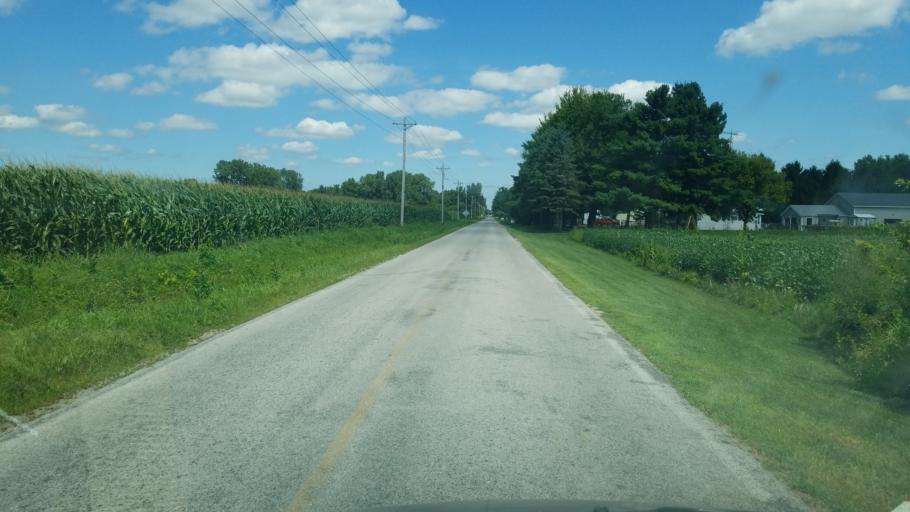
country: US
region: Ohio
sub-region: Fulton County
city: Delta
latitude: 41.5164
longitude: -83.9410
